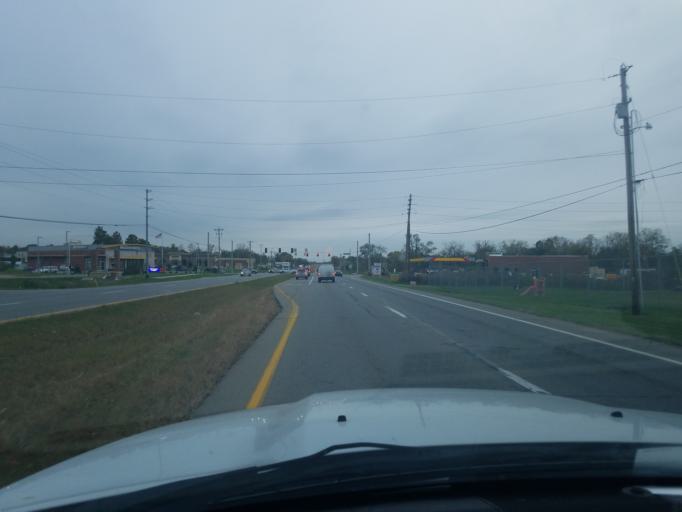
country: US
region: Indiana
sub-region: Clark County
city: Oak Park
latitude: 38.3589
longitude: -85.7013
